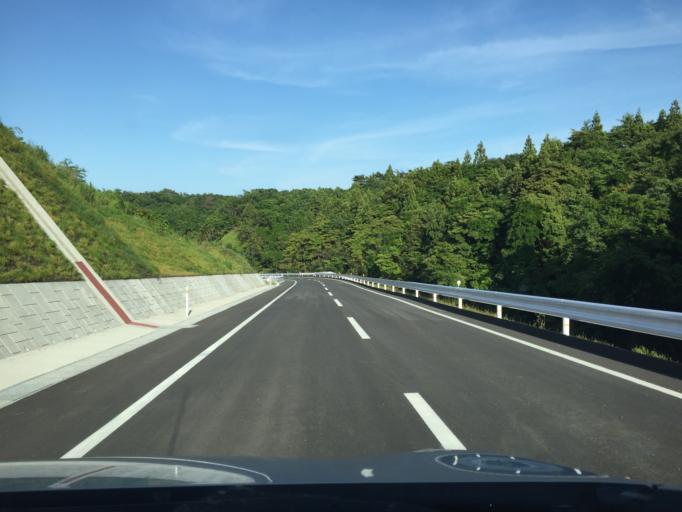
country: JP
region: Fukushima
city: Iwaki
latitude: 37.0004
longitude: 140.9716
